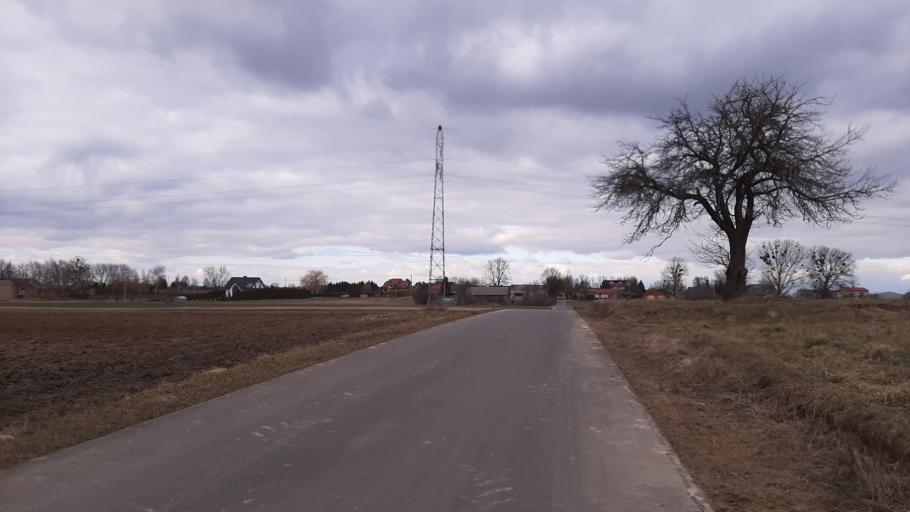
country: PL
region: Lublin Voivodeship
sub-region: Powiat lubelski
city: Jastkow
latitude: 51.3499
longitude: 22.3926
